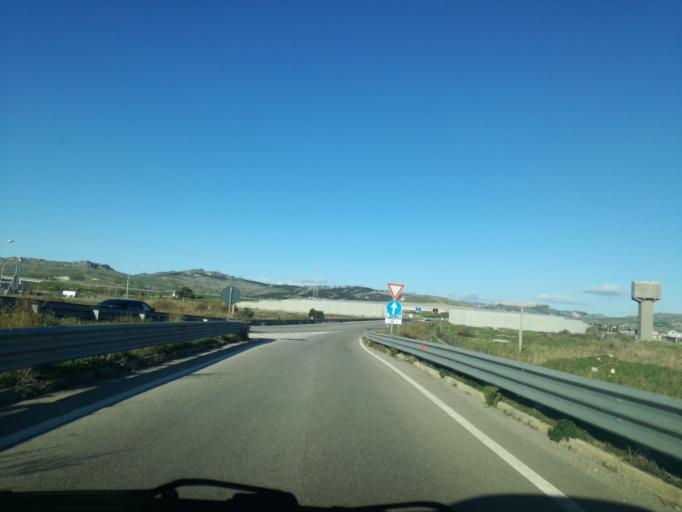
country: IT
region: Sicily
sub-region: Provincia di Caltanissetta
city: Butera
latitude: 37.1266
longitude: 14.1197
